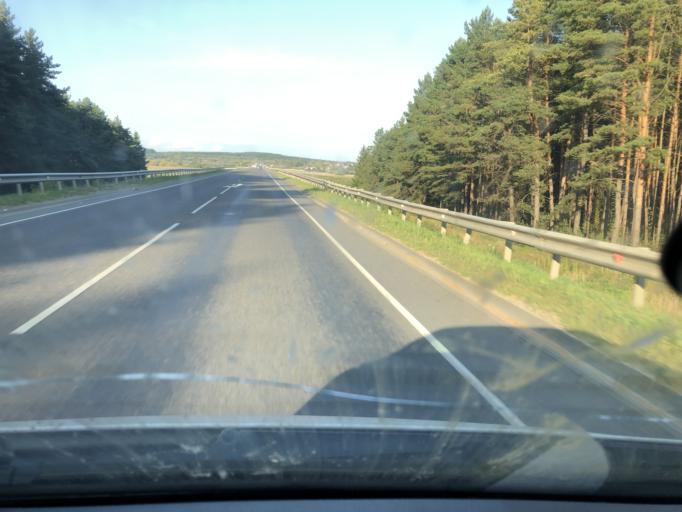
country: RU
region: Kaluga
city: Peremyshl'
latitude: 54.2837
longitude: 36.1556
